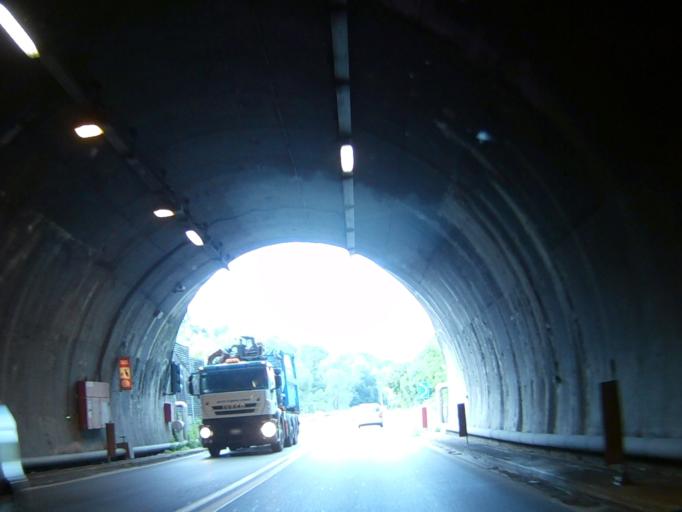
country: IT
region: Lombardy
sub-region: Provincia di Brescia
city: Gavardo-Sopraponte
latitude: 45.5864
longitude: 10.4542
